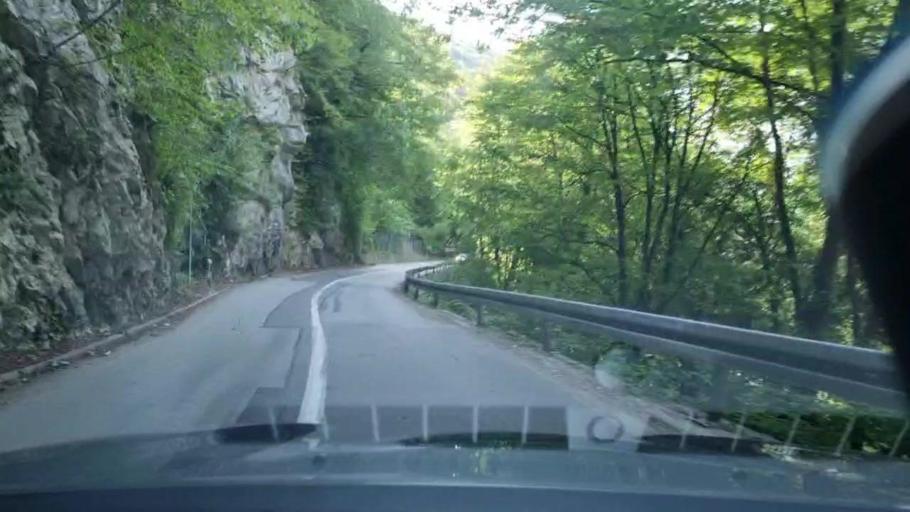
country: BA
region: Federation of Bosnia and Herzegovina
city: Bosanska Krupa
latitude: 44.8743
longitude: 16.0769
